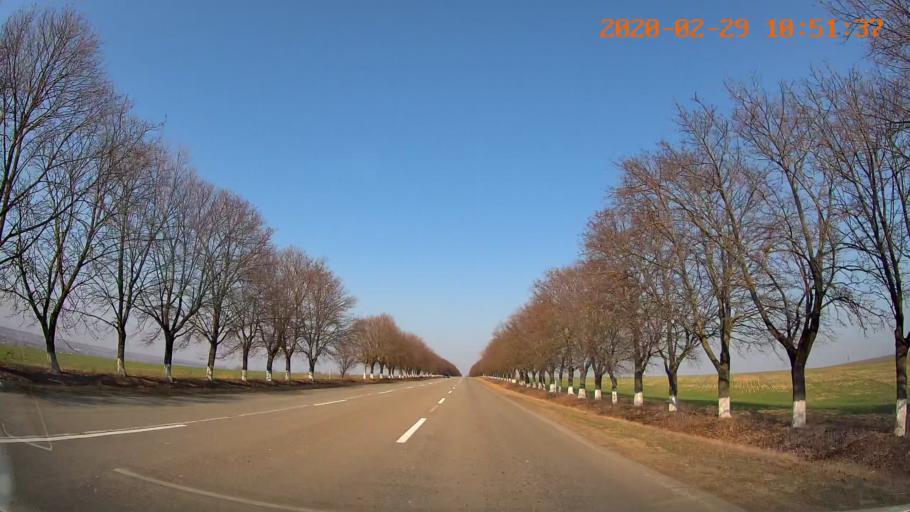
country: MD
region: Telenesti
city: Grigoriopol
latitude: 47.0952
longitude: 29.3619
